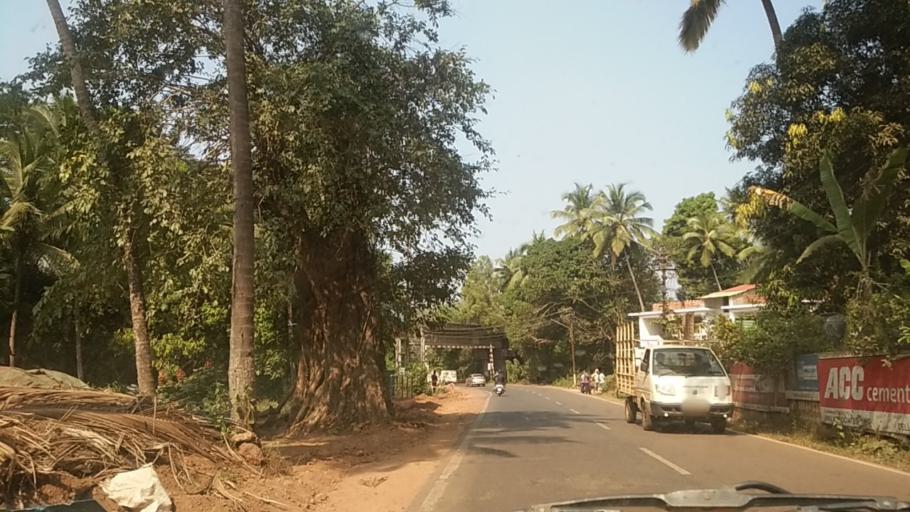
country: IN
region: Karnataka
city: Canacona
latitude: 15.0100
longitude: 74.0393
